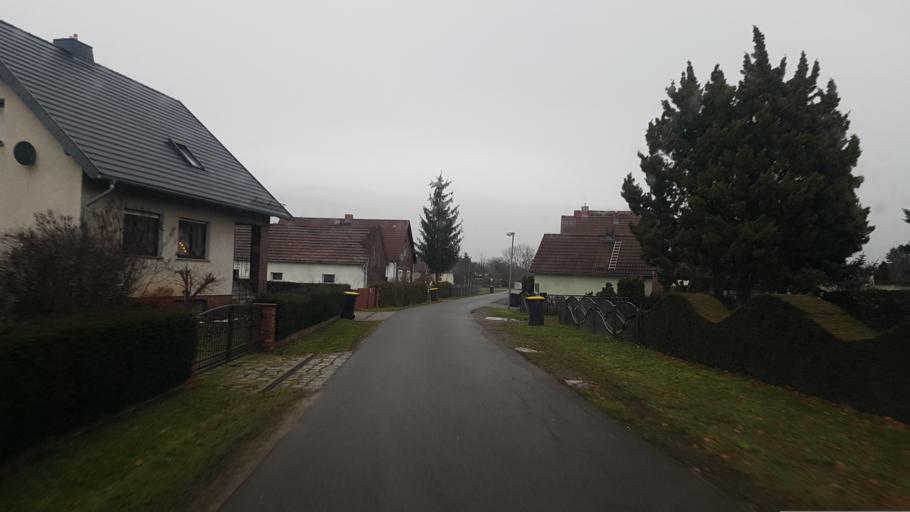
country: DE
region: Brandenburg
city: Drebkau
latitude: 51.6834
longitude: 14.2728
